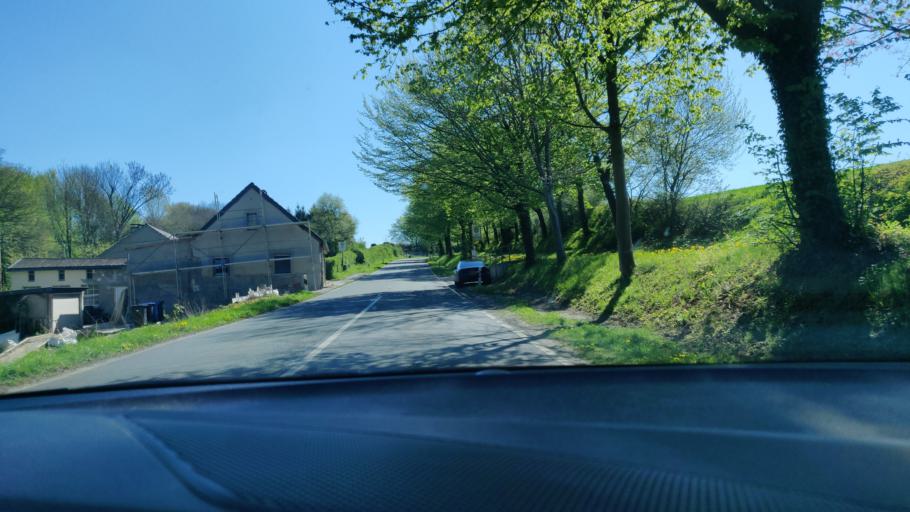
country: DE
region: North Rhine-Westphalia
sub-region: Regierungsbezirk Dusseldorf
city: Mettmann
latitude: 51.2371
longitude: 6.9898
